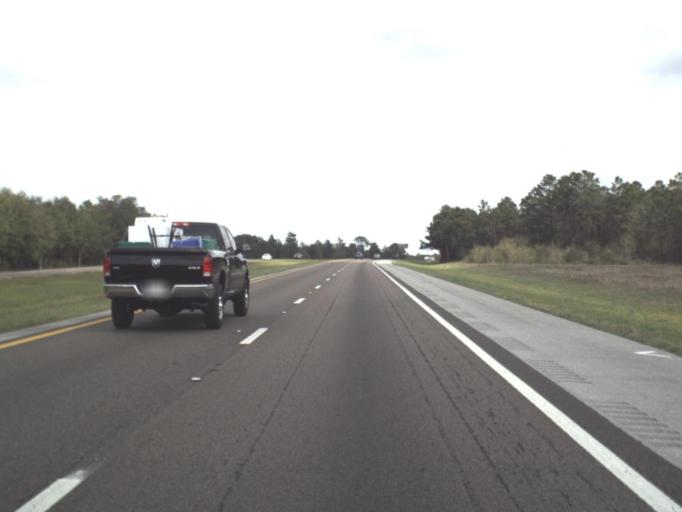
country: US
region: Florida
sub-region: Walton County
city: DeFuniak Springs
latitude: 30.7473
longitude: -86.2399
